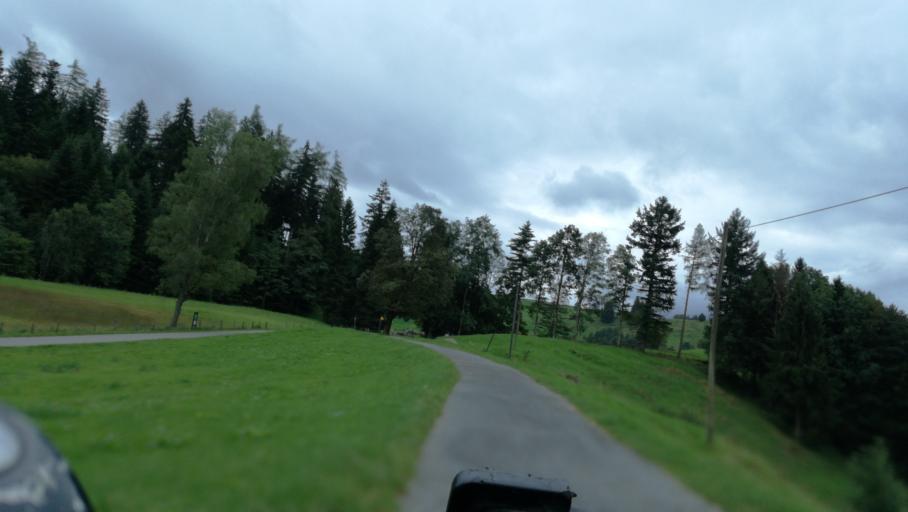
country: CH
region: Zug
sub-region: Zug
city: Zug
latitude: 47.1389
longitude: 8.5329
